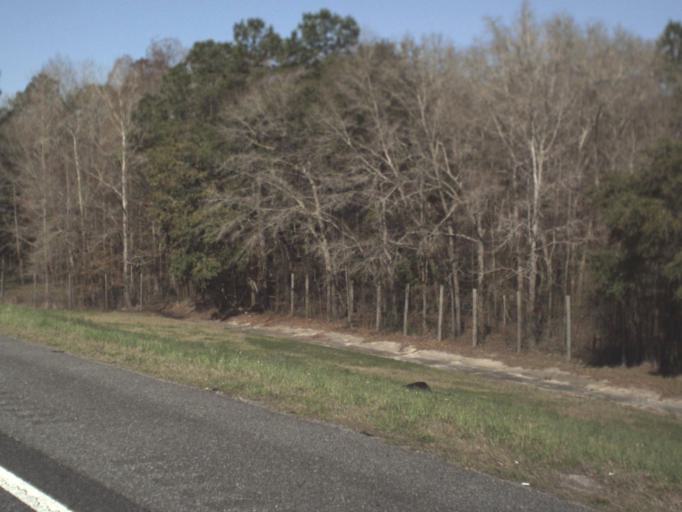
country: US
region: Florida
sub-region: Jefferson County
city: Monticello
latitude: 30.4823
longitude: -84.0482
